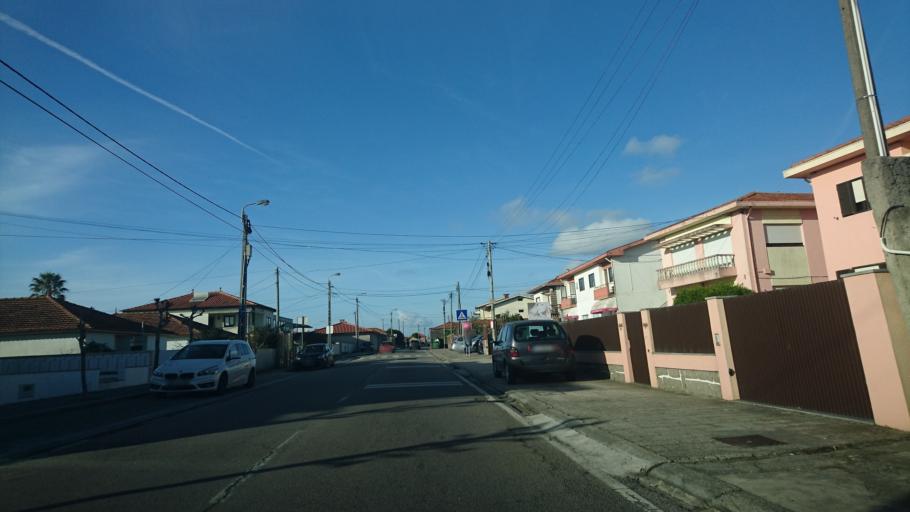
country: PT
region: Aveiro
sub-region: Espinho
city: Souto
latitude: 40.9815
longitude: -8.6320
